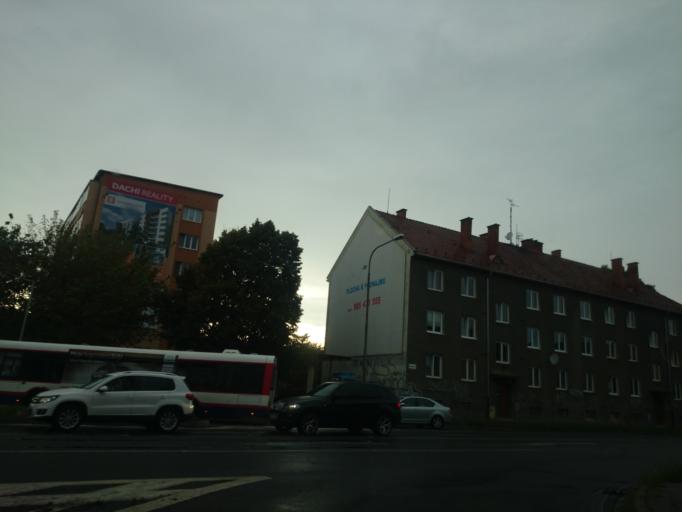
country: CZ
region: Olomoucky
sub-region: Okres Olomouc
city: Olomouc
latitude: 49.5813
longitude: 17.2570
